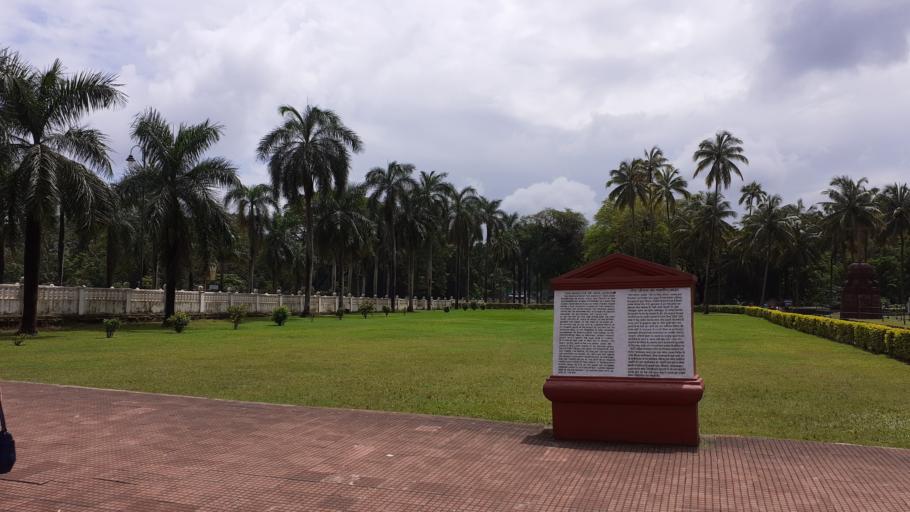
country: IN
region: Goa
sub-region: North Goa
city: Jua
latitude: 15.5013
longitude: 73.9115
